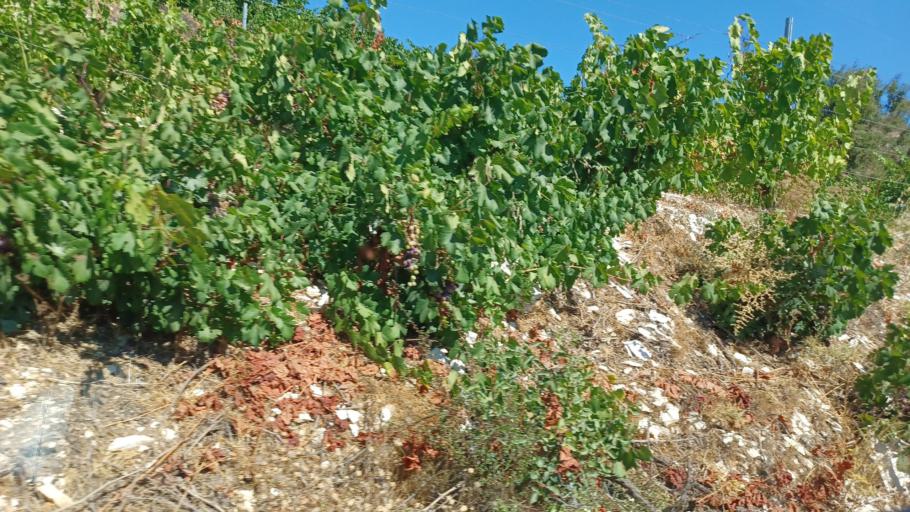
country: CY
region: Limassol
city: Pachna
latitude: 34.9047
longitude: 32.6368
